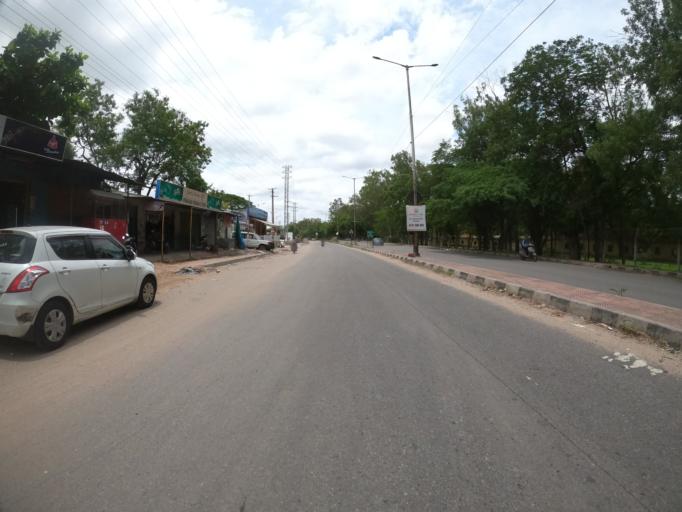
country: IN
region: Telangana
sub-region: Hyderabad
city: Hyderabad
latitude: 17.3788
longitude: 78.3703
